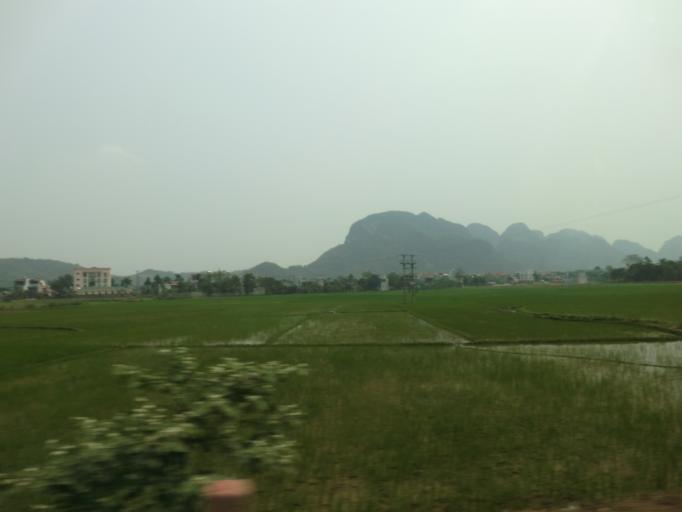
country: VN
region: Thanh Hoa
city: Thi Tran Ngoc Lac
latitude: 20.0854
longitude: 105.3737
